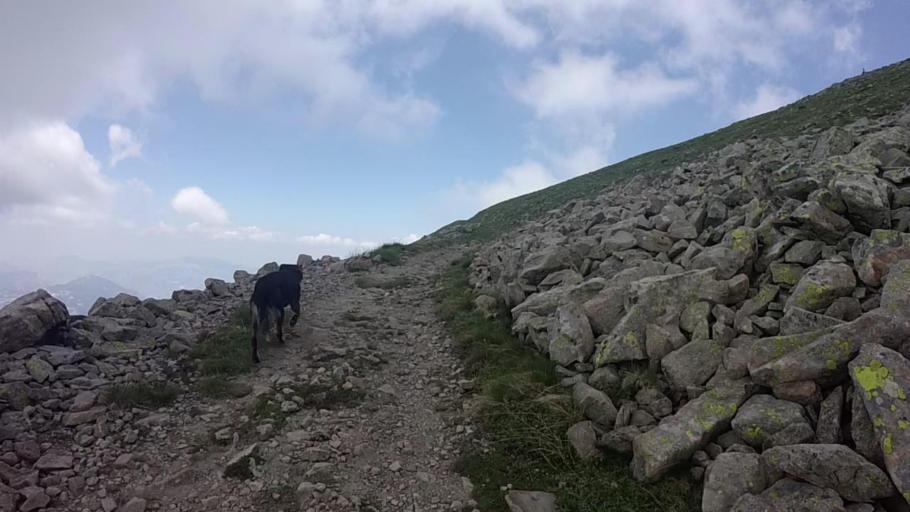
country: FR
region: Provence-Alpes-Cote d'Azur
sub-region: Departement des Alpes-de-Haute-Provence
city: Seyne-les-Alpes
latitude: 44.4103
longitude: 6.3845
